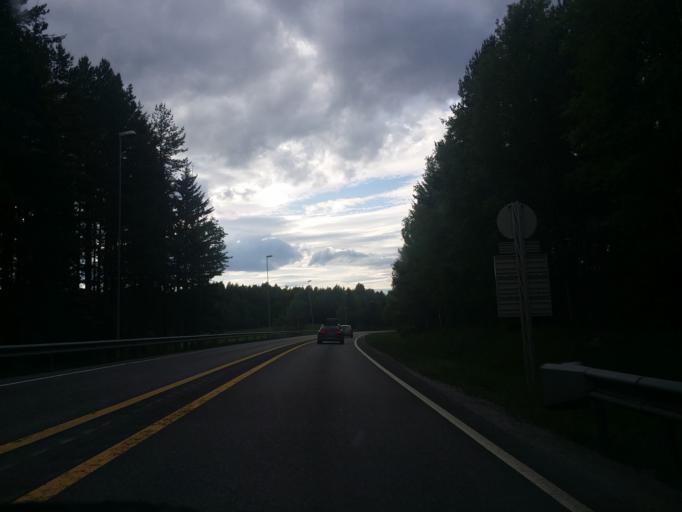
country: NO
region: Hedmark
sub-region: Ringsaker
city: Brumunddal
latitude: 60.8641
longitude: 10.9543
